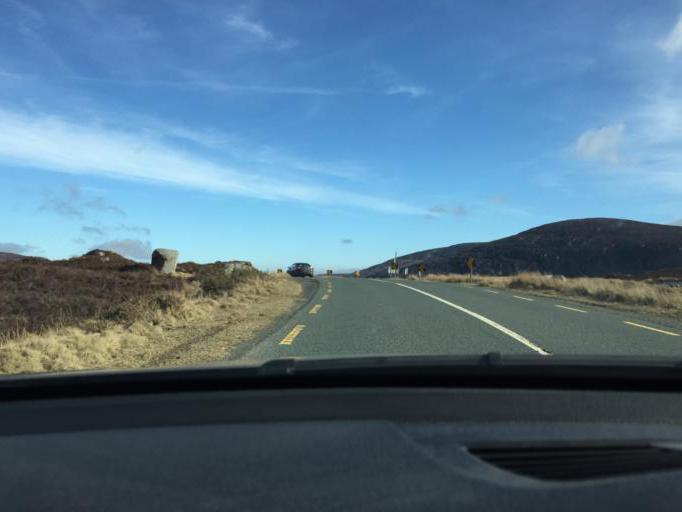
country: IE
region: Leinster
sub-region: Wicklow
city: Valleymount
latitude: 53.0423
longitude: -6.3985
